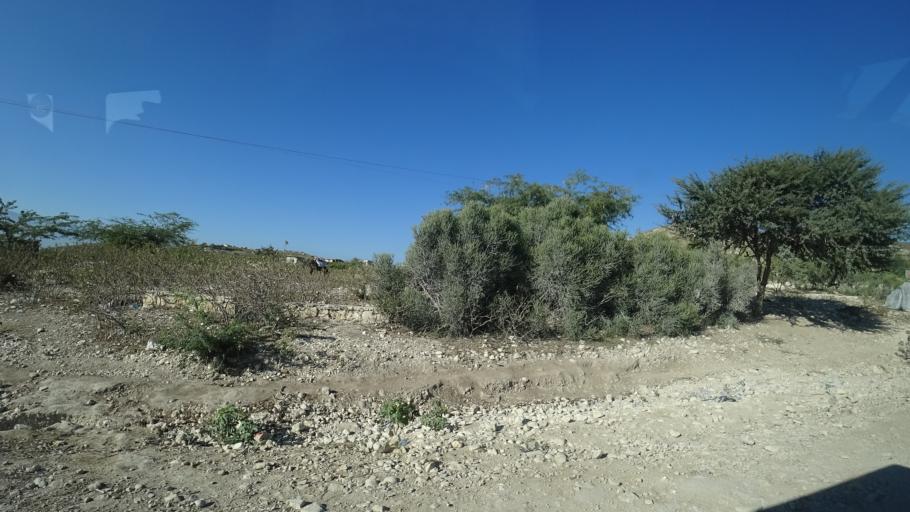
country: HT
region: Ouest
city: Croix des Bouquets
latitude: 18.6751
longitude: -72.2421
